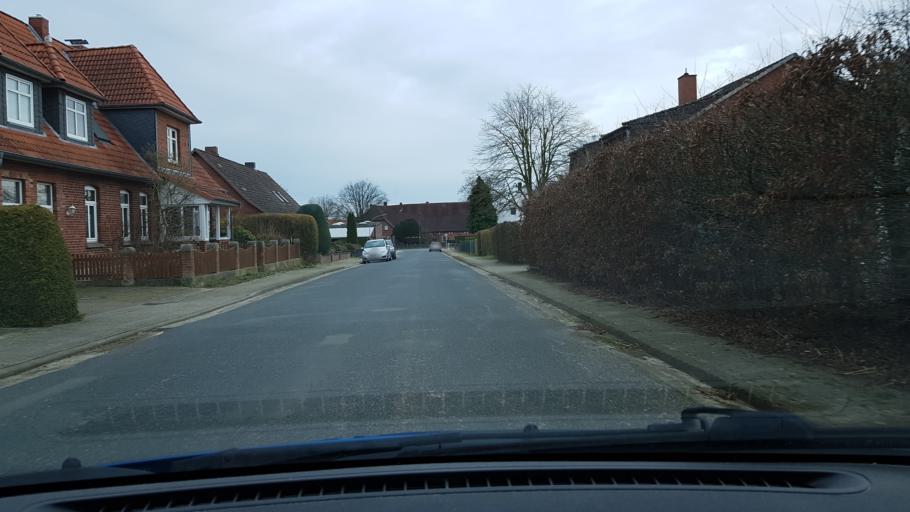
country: DE
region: Lower Saxony
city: Ratzlingen
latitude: 52.9773
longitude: 10.6683
